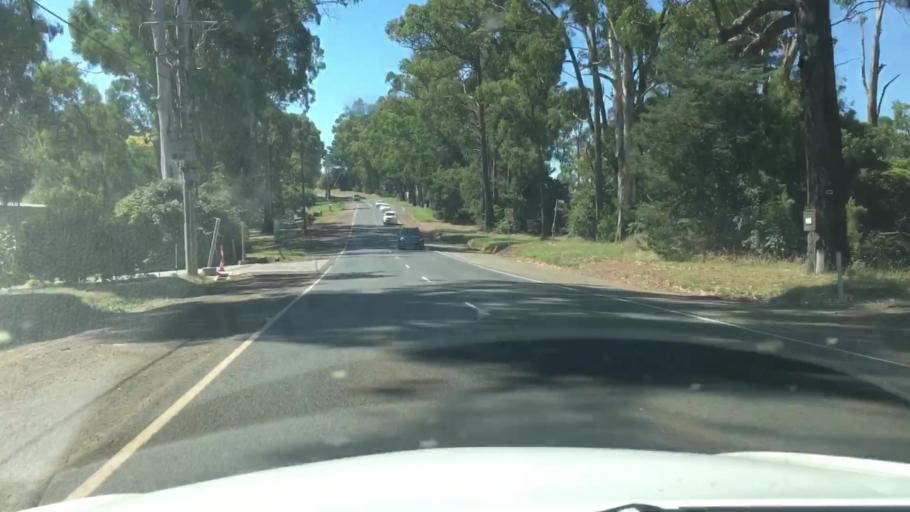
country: AU
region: Victoria
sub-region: Yarra Ranges
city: Mount Evelyn
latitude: -37.8093
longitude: 145.4056
